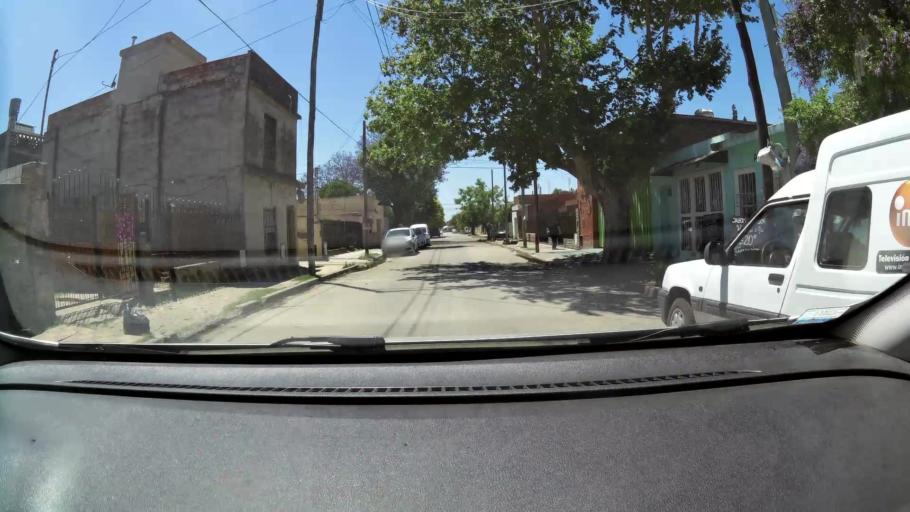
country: AR
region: Cordoba
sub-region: Departamento de Capital
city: Cordoba
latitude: -31.4285
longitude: -64.1163
